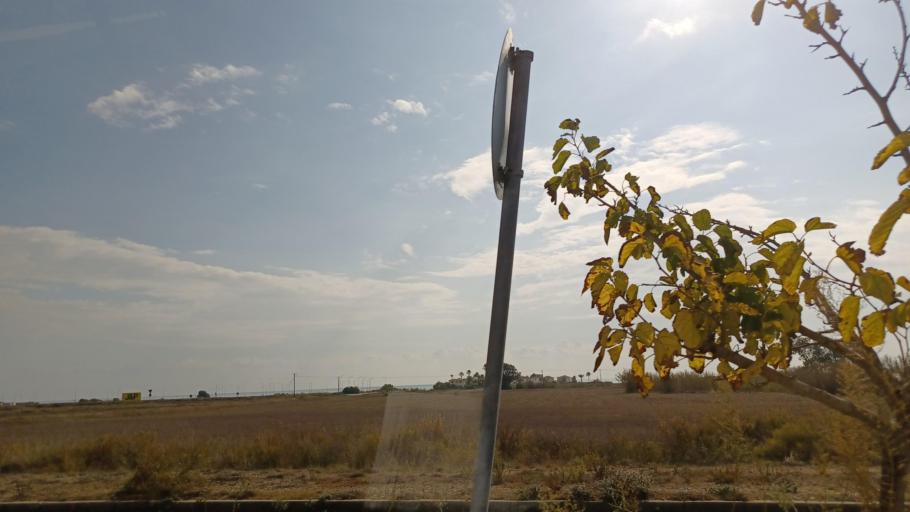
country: CY
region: Larnaka
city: Perivolia
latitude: 34.8260
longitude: 33.5606
